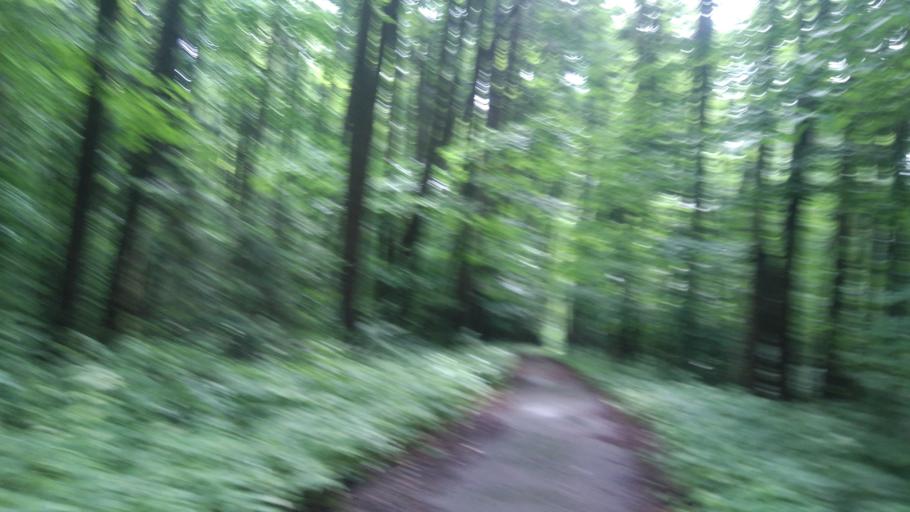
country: RU
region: Perm
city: Ferma
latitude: 57.9635
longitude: 56.3400
